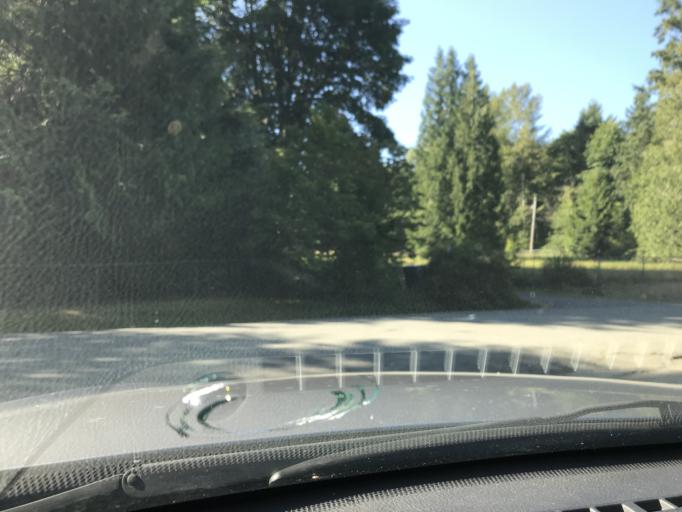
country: US
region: Washington
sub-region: King County
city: Maple Heights-Lake Desire
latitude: 47.4371
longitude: -122.0939
